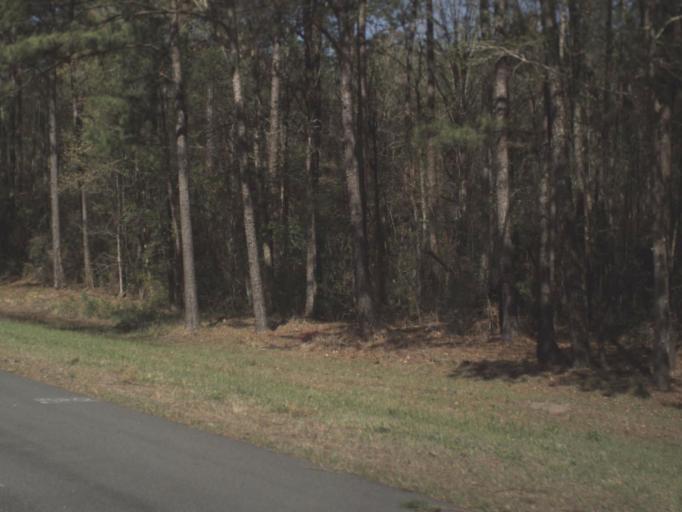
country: US
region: Florida
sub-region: Walton County
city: DeFuniak Springs
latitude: 30.7007
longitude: -85.9710
